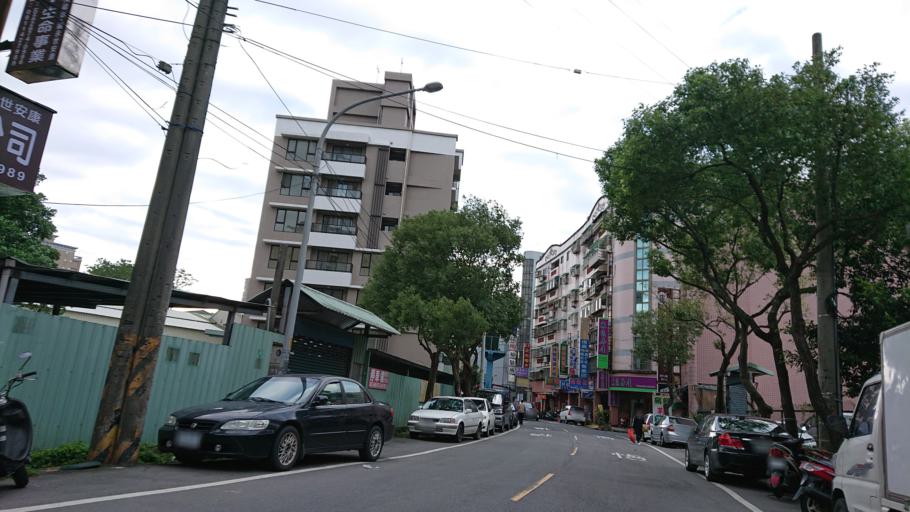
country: TW
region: Taiwan
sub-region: Taoyuan
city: Taoyuan
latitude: 24.9330
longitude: 121.3771
